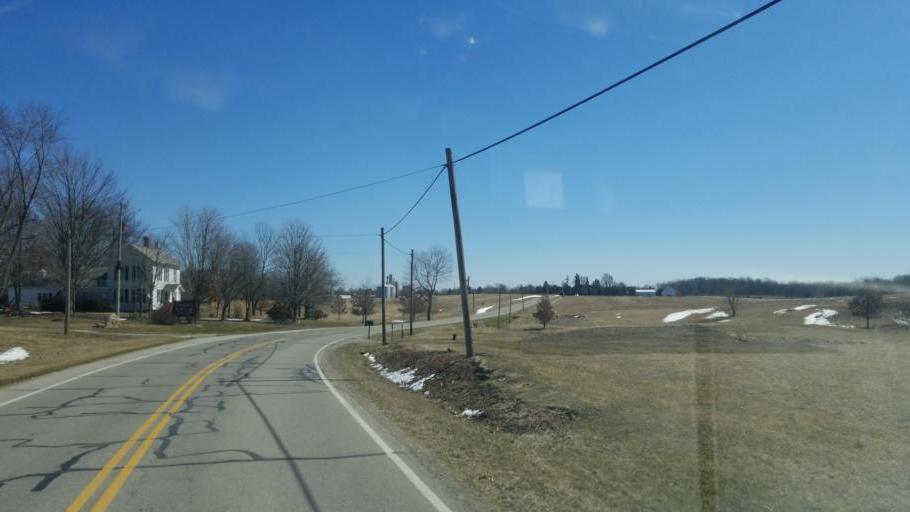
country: US
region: Ohio
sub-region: Crawford County
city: Bucyrus
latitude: 40.8069
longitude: -83.0050
